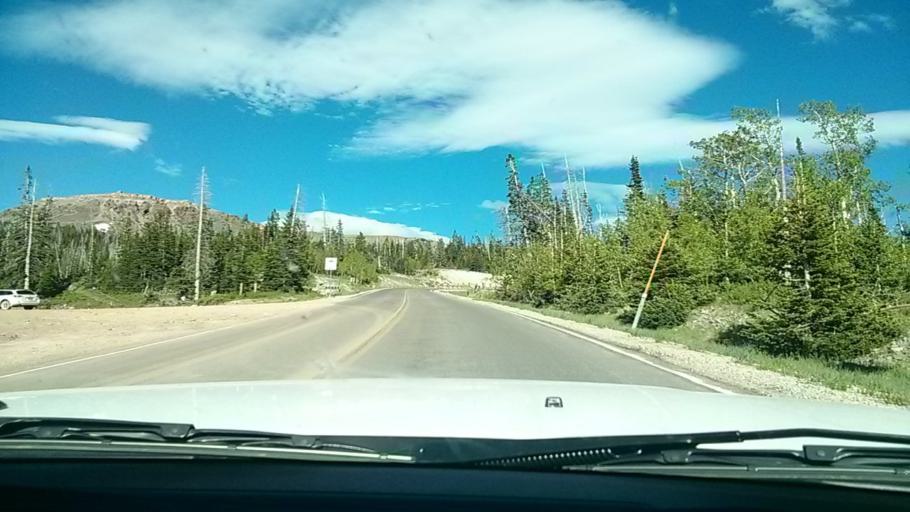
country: US
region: Utah
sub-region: Iron County
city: Parowan
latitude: 37.6773
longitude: -112.8458
